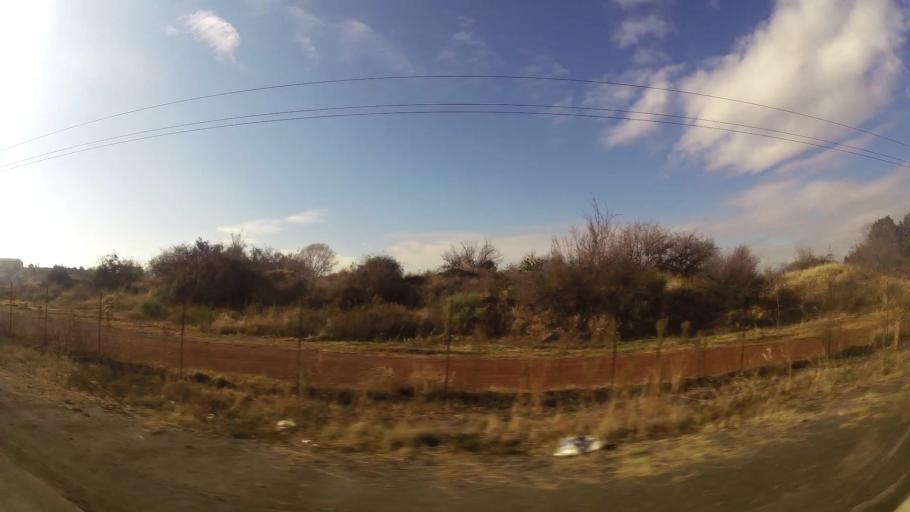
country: ZA
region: Gauteng
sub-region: Sedibeng District Municipality
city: Meyerton
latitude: -26.5140
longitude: 28.0512
